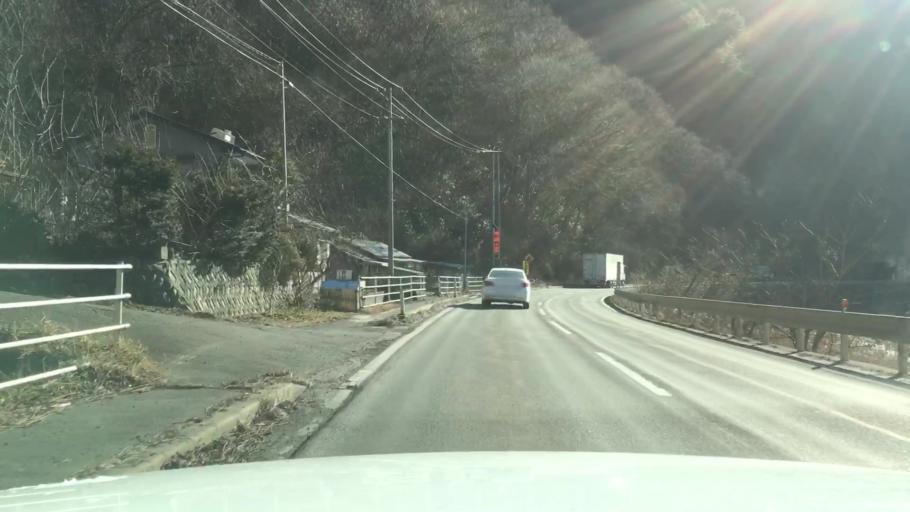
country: JP
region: Iwate
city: Miyako
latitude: 39.6081
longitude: 141.6515
